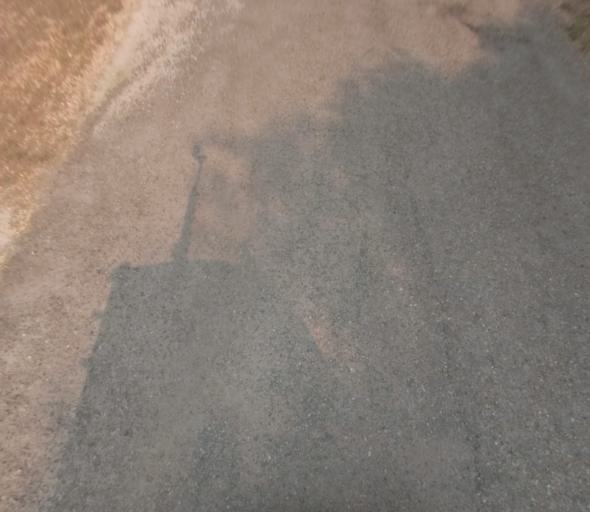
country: US
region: California
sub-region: Madera County
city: Oakhurst
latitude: 37.3080
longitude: -119.6280
